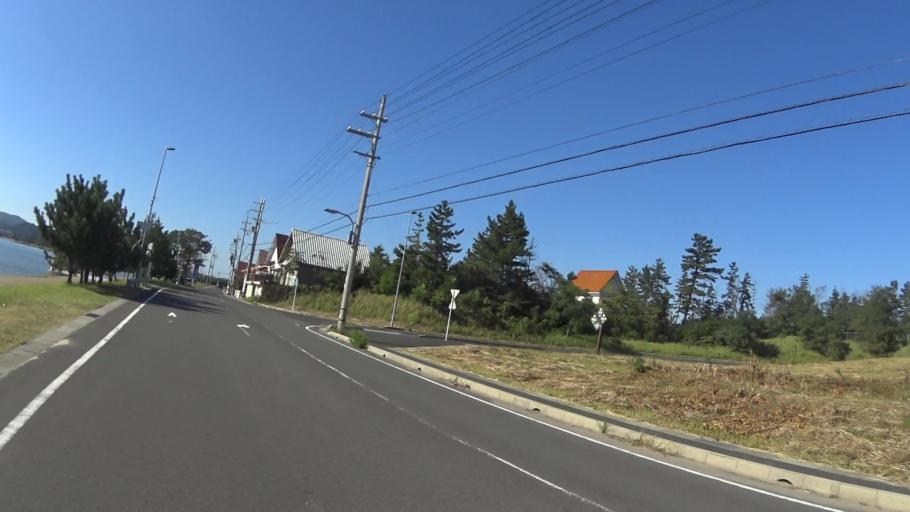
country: JP
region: Hyogo
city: Toyooka
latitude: 35.6400
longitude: 134.9238
